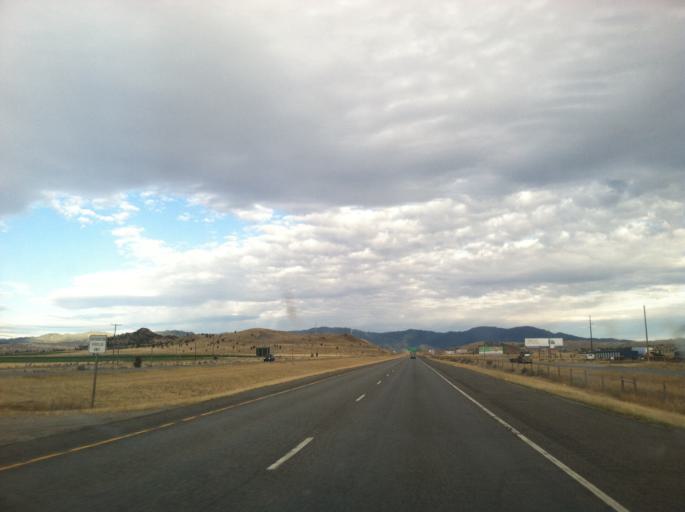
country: US
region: Montana
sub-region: Silver Bow County
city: Butte-Silver Bow (Balance)
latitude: 46.0088
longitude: -112.6748
